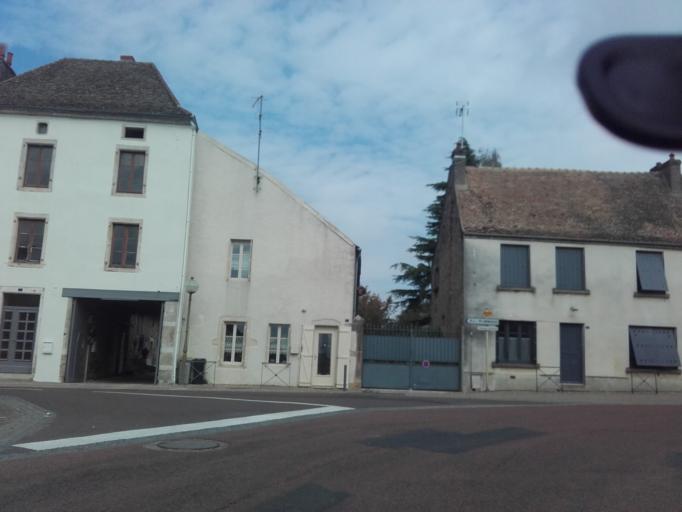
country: FR
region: Bourgogne
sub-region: Departement de la Cote-d'Or
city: Bligny-les-Beaune
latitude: 46.9858
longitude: 4.8239
